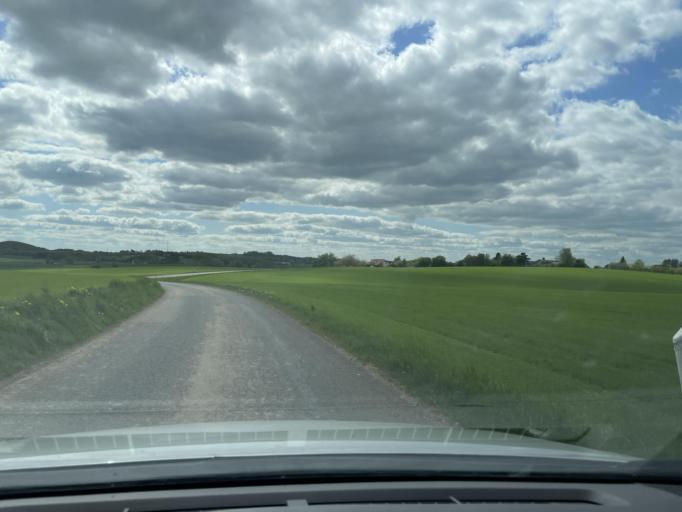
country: DK
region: Central Jutland
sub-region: Skanderborg Kommune
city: Skanderborg
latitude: 55.9257
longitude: 9.9921
